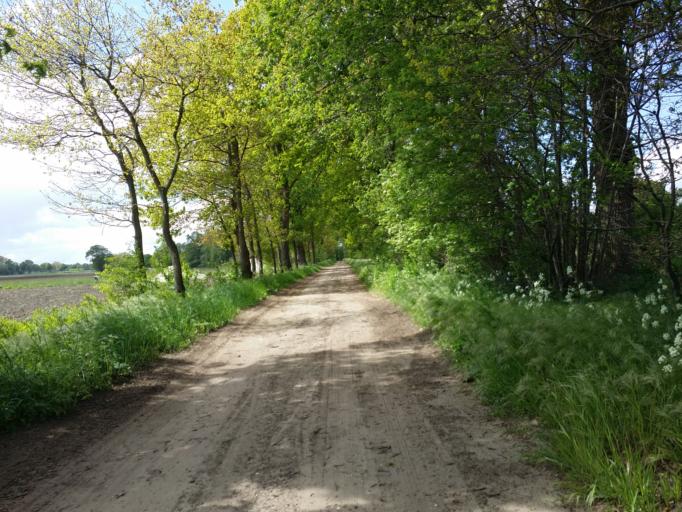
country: DE
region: Lower Saxony
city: Gross Ippener
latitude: 52.9844
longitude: 8.6291
